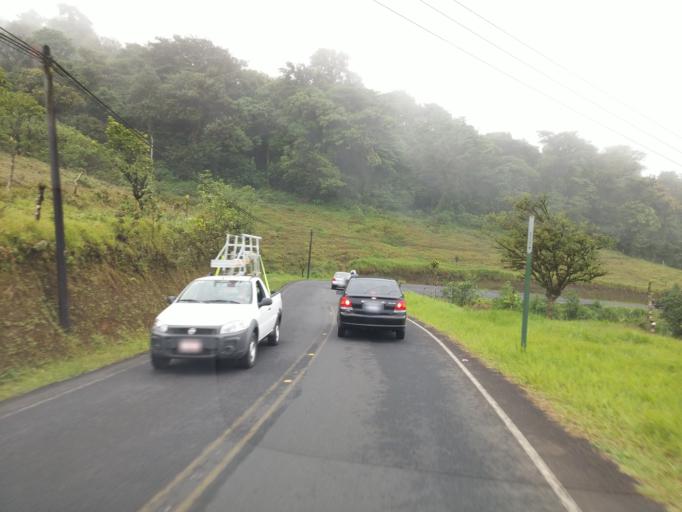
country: CR
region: Alajuela
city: San Ramon
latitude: 10.1677
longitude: -84.4926
